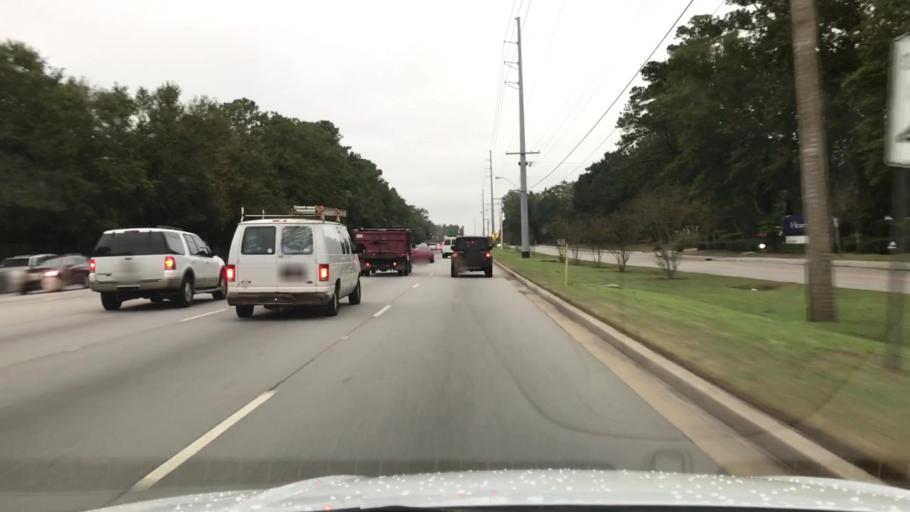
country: US
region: South Carolina
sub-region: Charleston County
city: North Charleston
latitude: 32.8231
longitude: -79.9914
